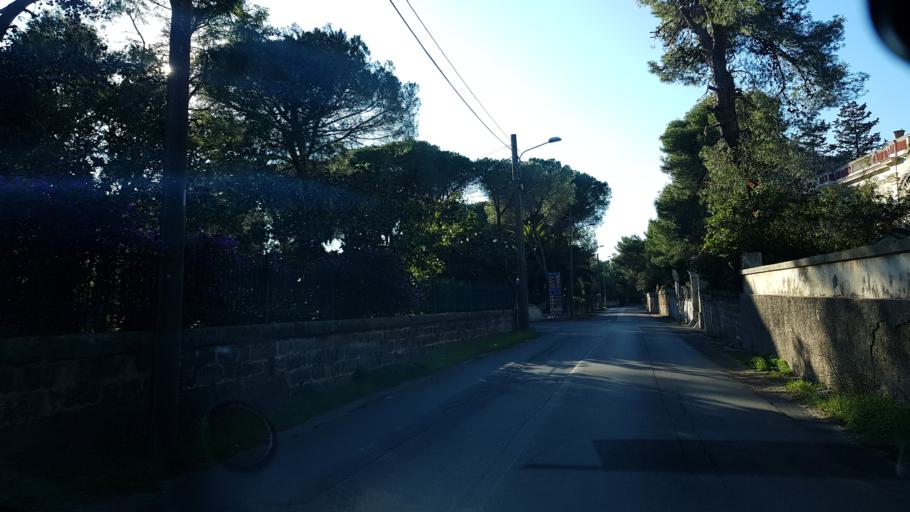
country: IT
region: Apulia
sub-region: Provincia di Lecce
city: Nardo
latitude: 40.1472
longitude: 17.9966
